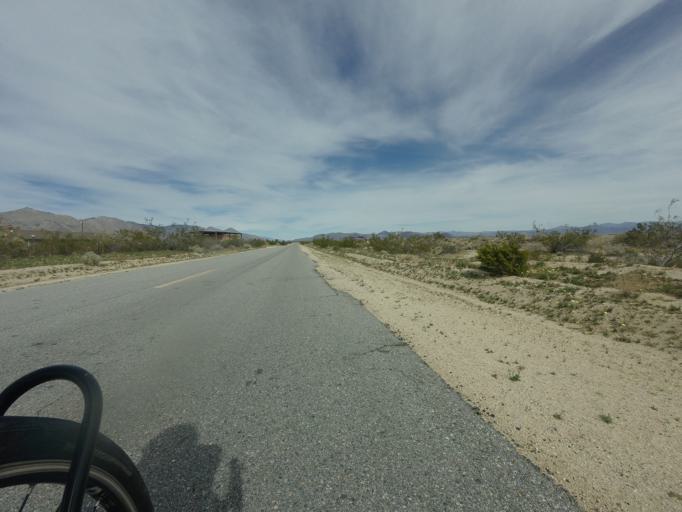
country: US
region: California
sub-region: Kern County
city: Inyokern
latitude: 35.7643
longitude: -117.8472
